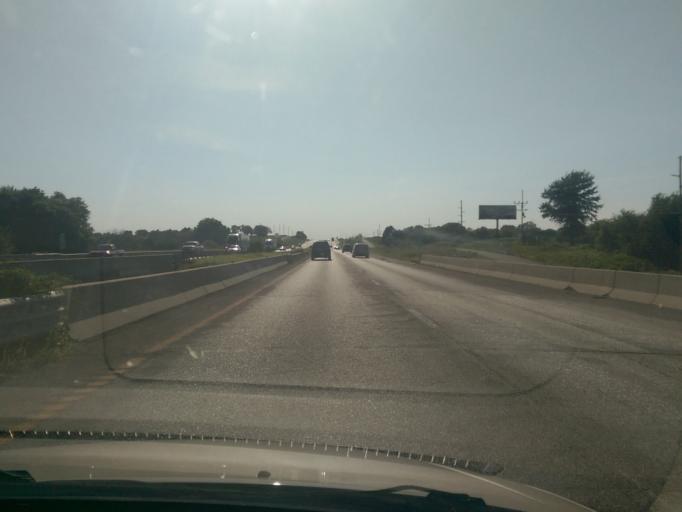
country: US
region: Missouri
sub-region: Lafayette County
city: Odessa
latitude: 39.0037
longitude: -93.8349
